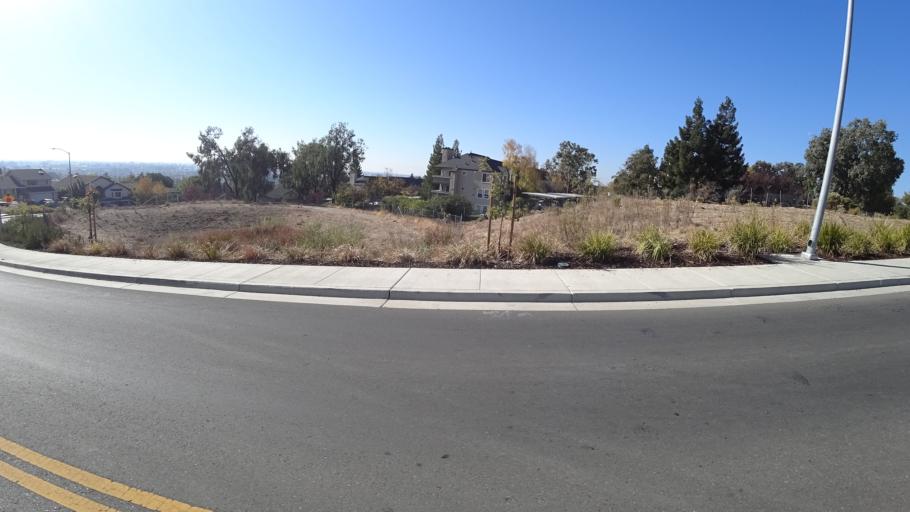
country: US
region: California
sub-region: Alameda County
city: Fairview
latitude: 37.6337
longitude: -122.0435
